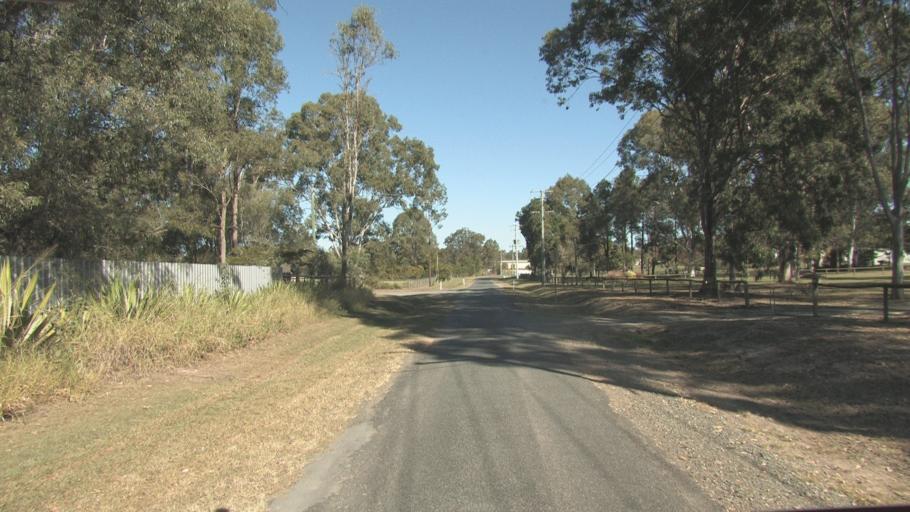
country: AU
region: Queensland
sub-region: Logan
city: Waterford West
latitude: -27.7216
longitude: 153.1255
